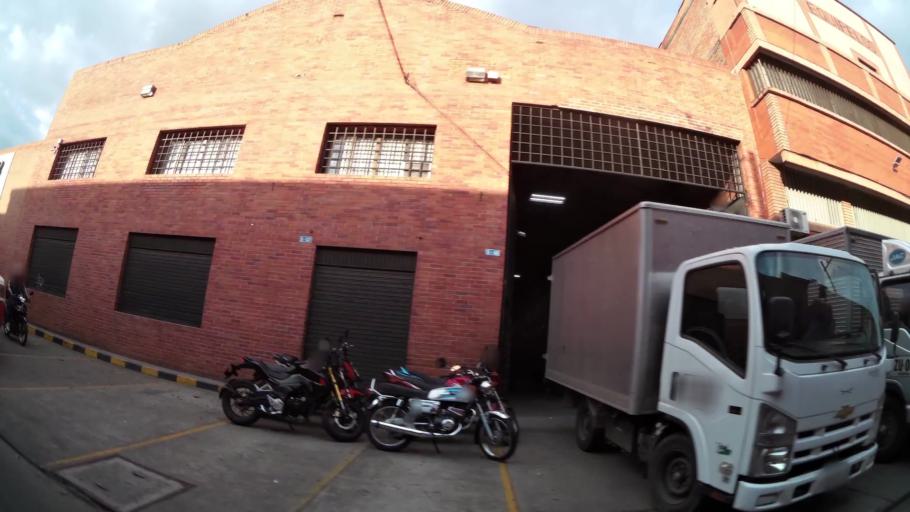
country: CO
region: Valle del Cauca
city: Cali
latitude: 3.4557
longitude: -76.5222
